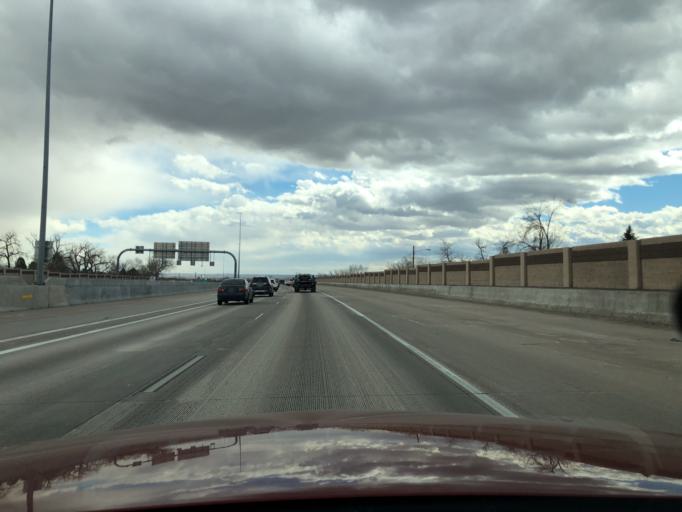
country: US
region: Colorado
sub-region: Adams County
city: Westminster
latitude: 39.8412
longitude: -105.0385
